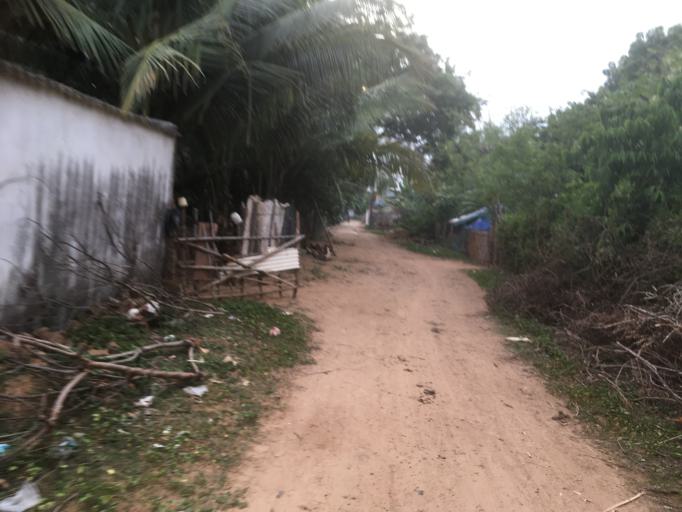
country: IN
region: Tamil Nadu
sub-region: Villupuram
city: Auroville
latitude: 12.0116
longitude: 79.8015
